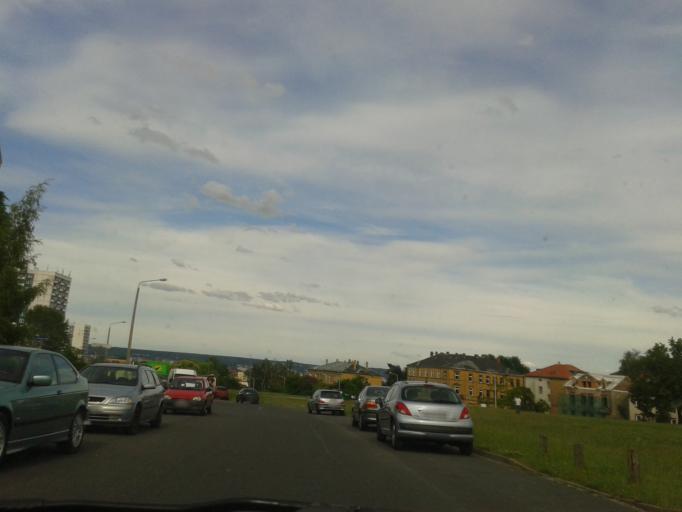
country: DE
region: Saxony
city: Freital
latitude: 51.0413
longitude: 13.6734
